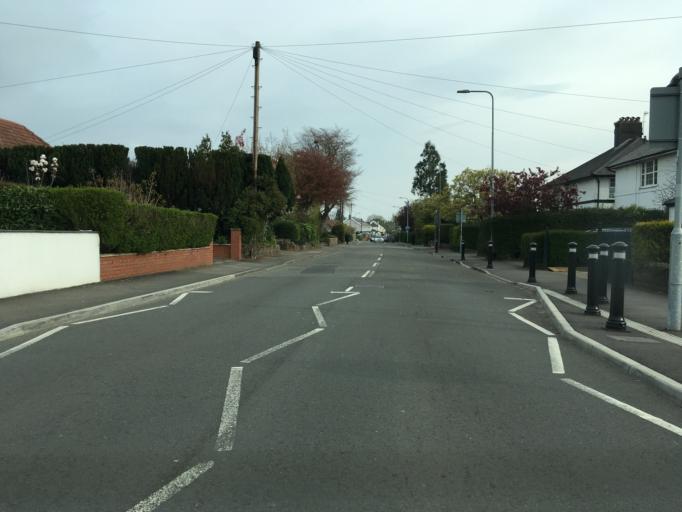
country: GB
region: Wales
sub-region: Cardiff
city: Radyr
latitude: 51.5248
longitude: -3.2147
